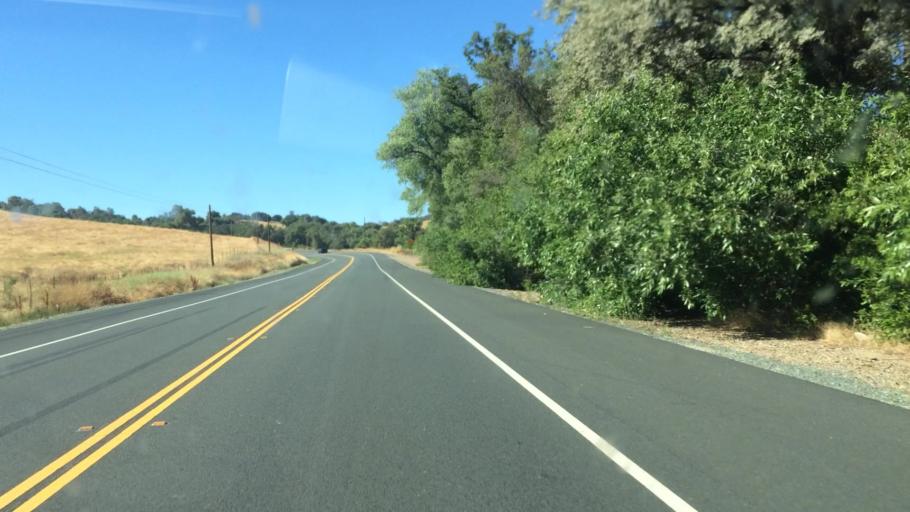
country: US
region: California
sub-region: El Dorado County
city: Deer Park
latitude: 38.6547
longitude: -120.8538
